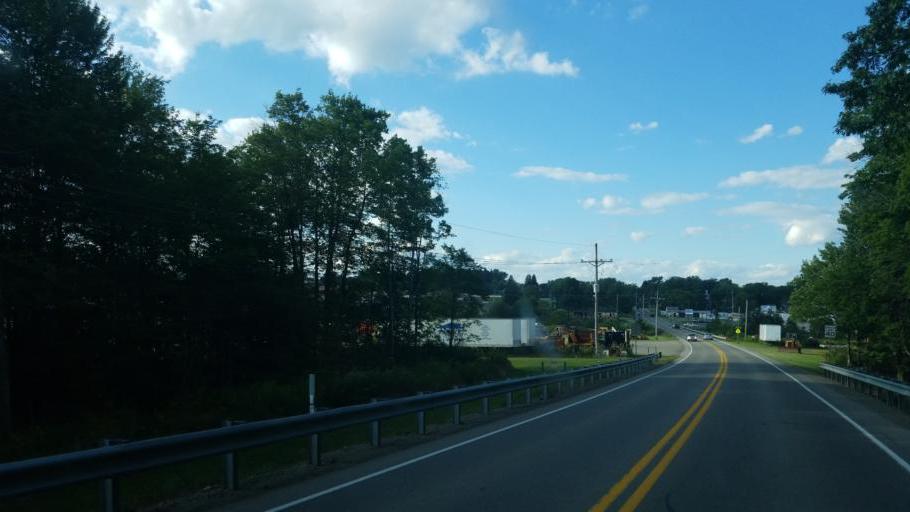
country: US
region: Pennsylvania
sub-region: Clarion County
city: Knox
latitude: 41.2267
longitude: -79.5289
